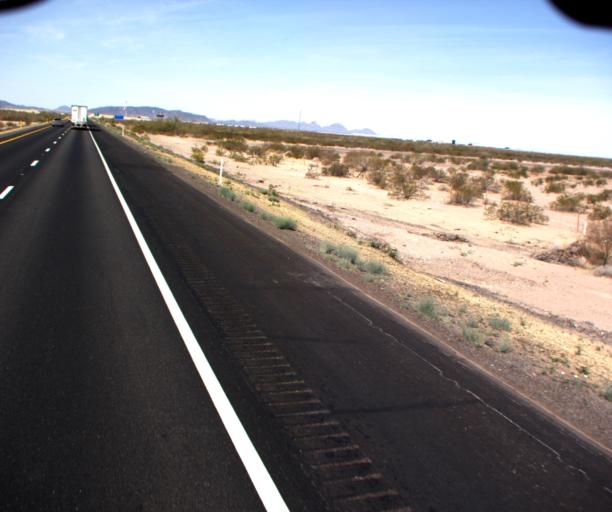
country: US
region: Arizona
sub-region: La Paz County
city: Salome
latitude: 33.6292
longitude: -113.7536
